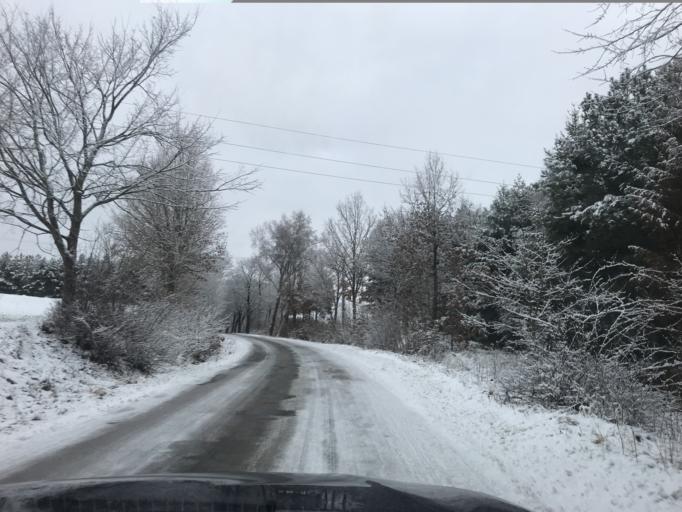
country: PL
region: Pomeranian Voivodeship
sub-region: Powiat bytowski
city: Parchowo
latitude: 54.2350
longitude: 17.5748
